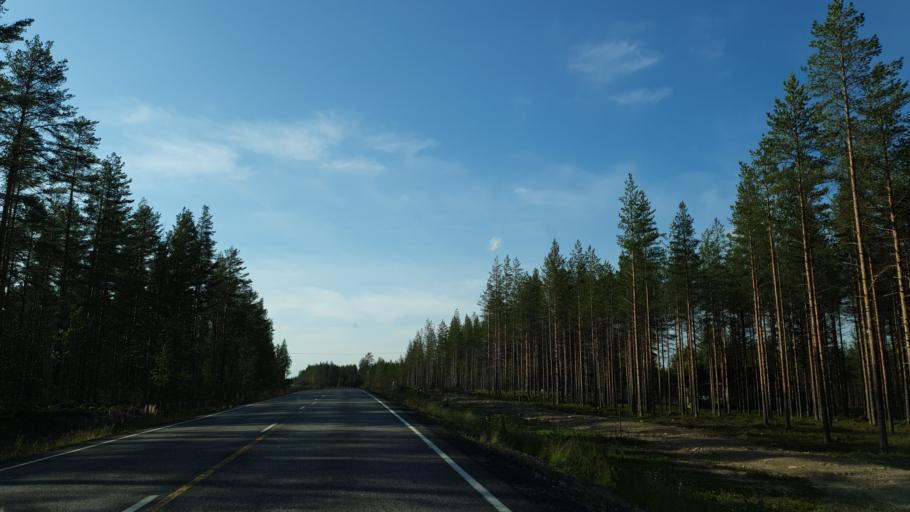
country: FI
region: Kainuu
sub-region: Kehys-Kainuu
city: Kuhmo
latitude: 64.0903
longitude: 29.4811
